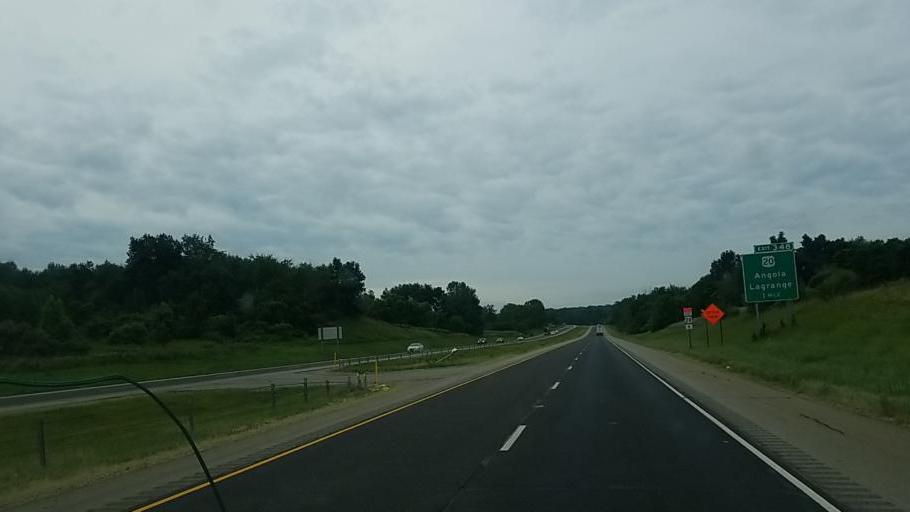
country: US
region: Indiana
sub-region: Steuben County
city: Angola
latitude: 41.6549
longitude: -85.0415
